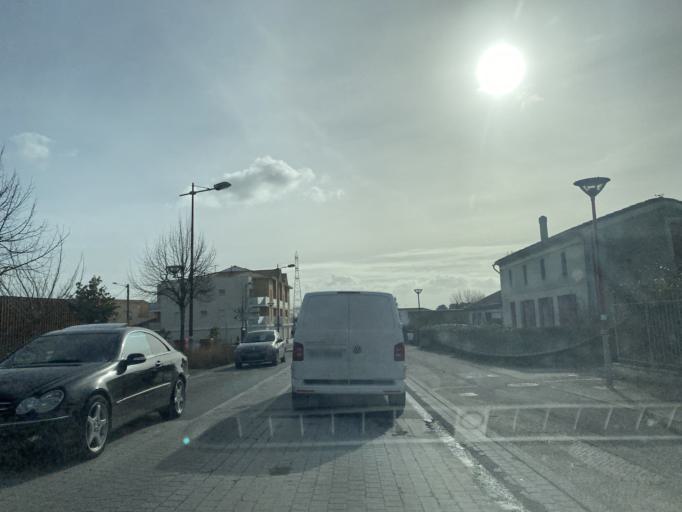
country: FR
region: Aquitaine
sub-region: Departement de la Gironde
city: Le Taillan-Medoc
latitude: 44.9037
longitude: -0.6691
